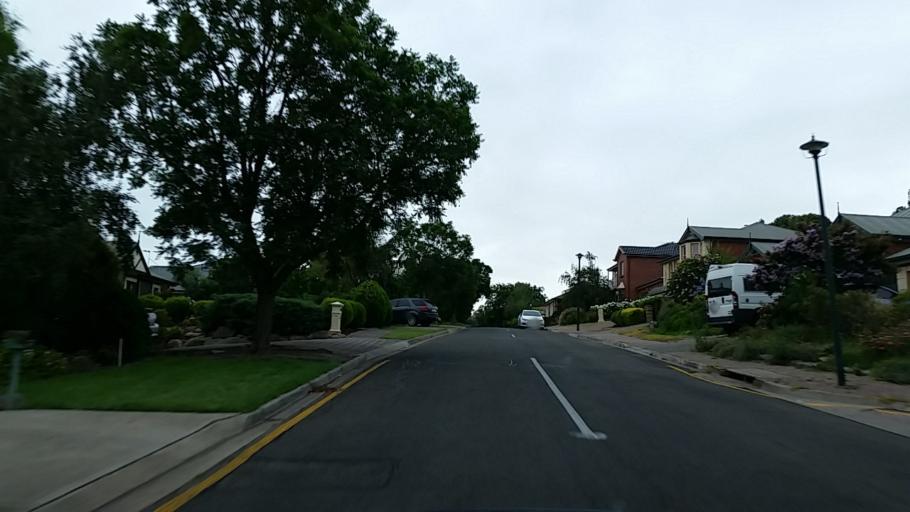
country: AU
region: South Australia
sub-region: Campbelltown
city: Athelstone
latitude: -34.8661
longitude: 138.6934
